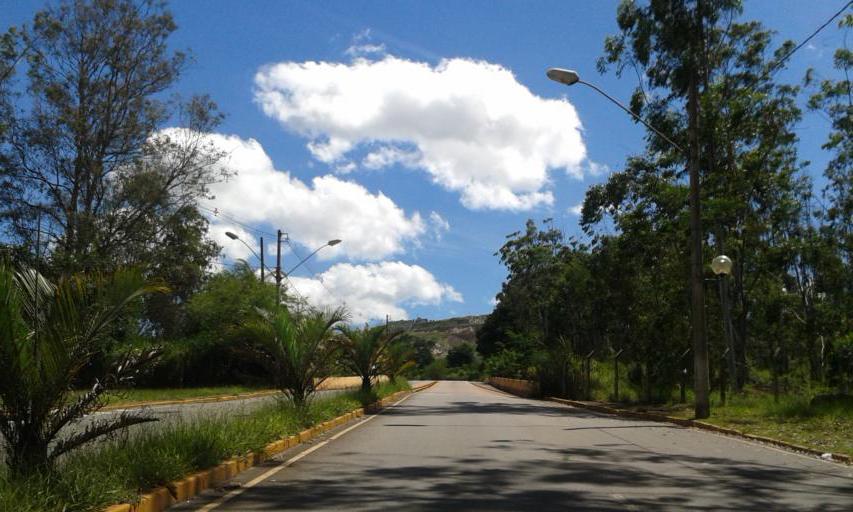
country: BR
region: Minas Gerais
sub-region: Itabira
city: Itabira
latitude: -19.6354
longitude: -43.2403
